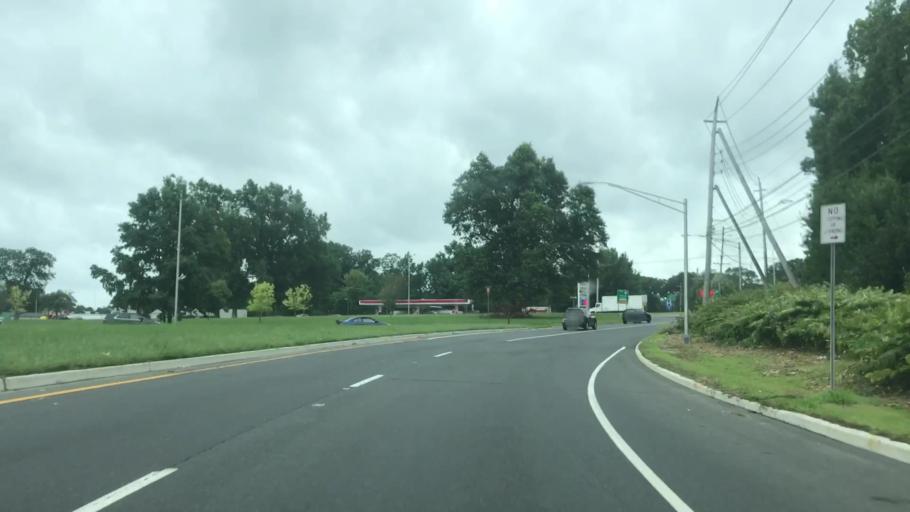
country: US
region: New Jersey
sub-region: Monmouth County
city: Wanamassa
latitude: 40.2277
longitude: -74.0392
